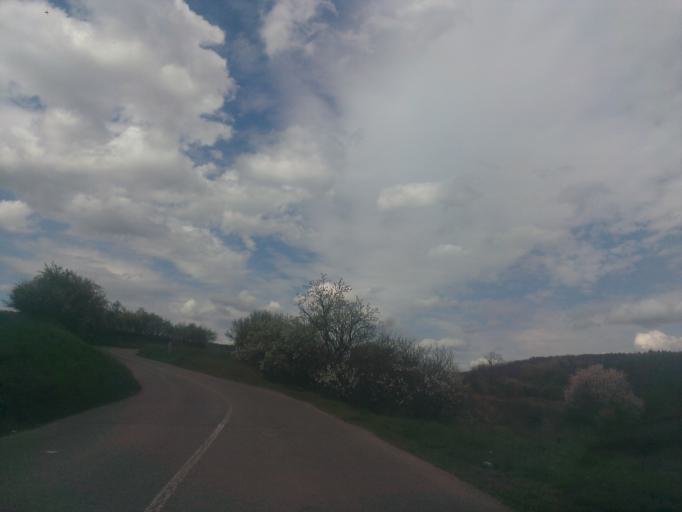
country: CZ
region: South Moravian
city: Dolni Kounice
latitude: 49.0925
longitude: 16.4425
